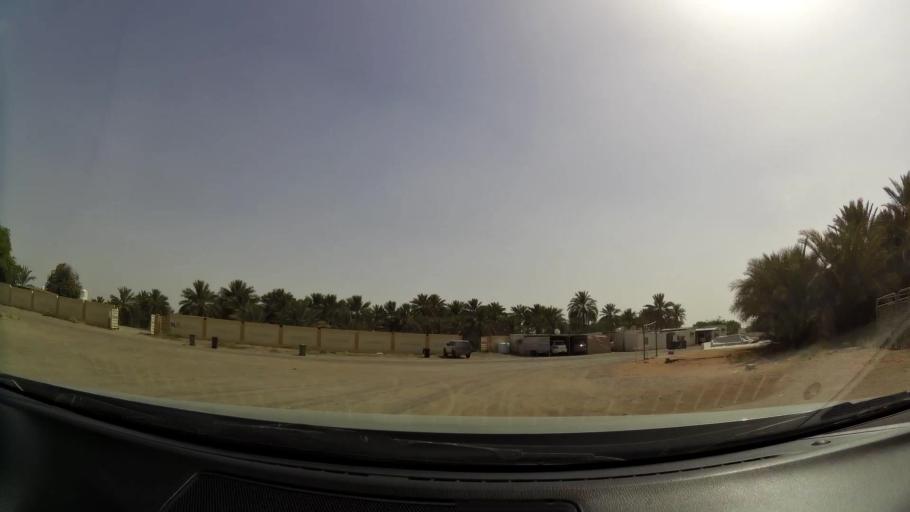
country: AE
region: Abu Dhabi
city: Al Ain
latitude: 24.2294
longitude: 55.6874
